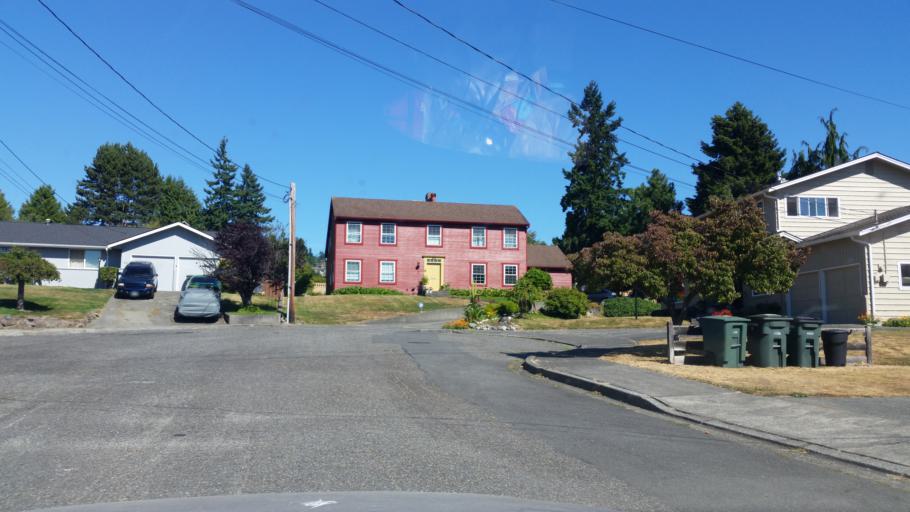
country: US
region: Washington
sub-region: Snohomish County
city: Edmonds
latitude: 47.8189
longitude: -122.3689
